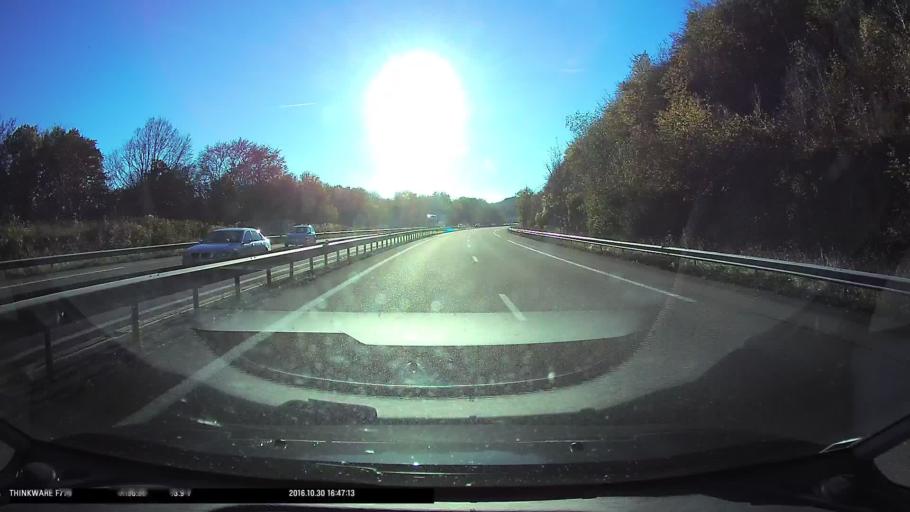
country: FR
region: Franche-Comte
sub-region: Departement du Doubs
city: Chatillon-le-Duc
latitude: 47.2879
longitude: 6.0111
